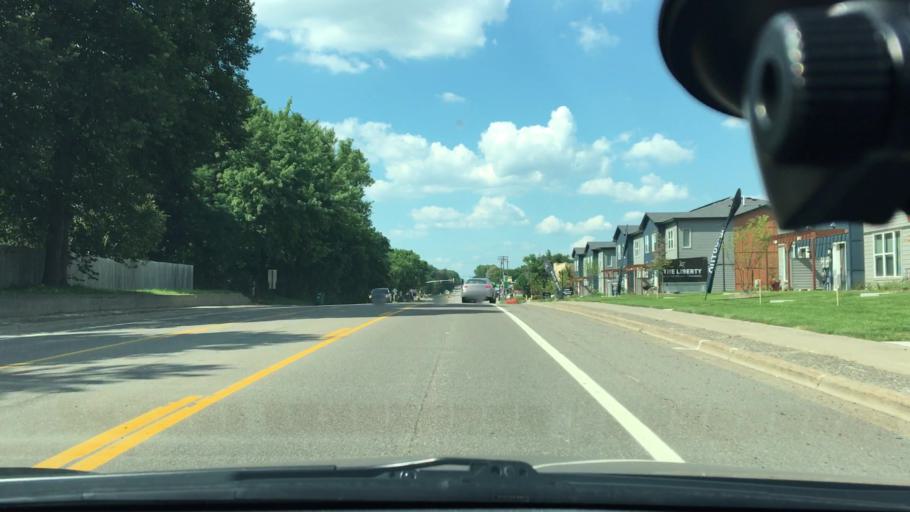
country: US
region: Minnesota
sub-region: Hennepin County
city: Golden Valley
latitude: 45.0047
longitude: -93.3803
